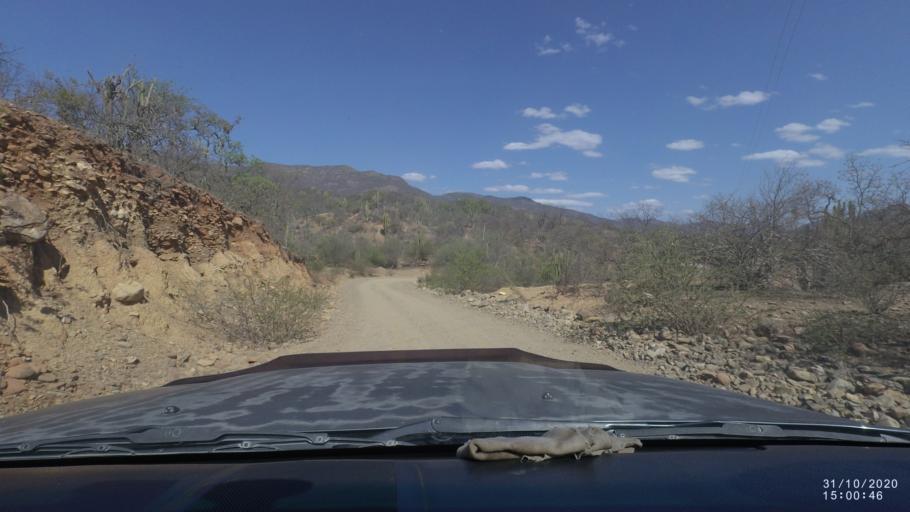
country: BO
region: Cochabamba
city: Aiquile
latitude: -18.2598
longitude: -64.8228
